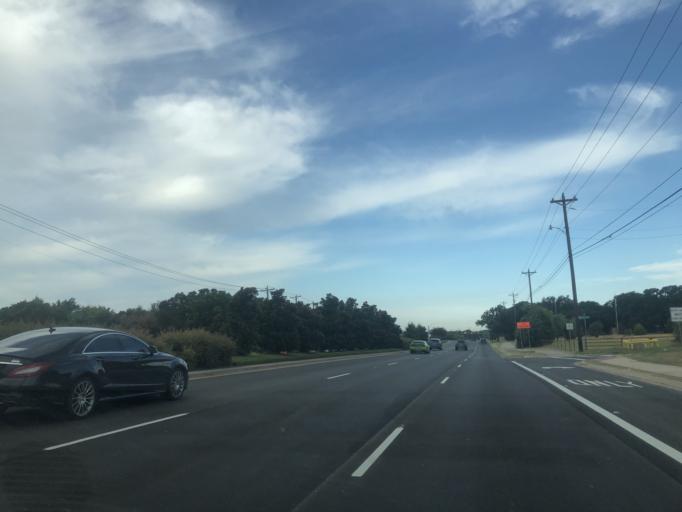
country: US
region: Texas
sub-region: Tarrant County
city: Southlake
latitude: 32.9352
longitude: -97.1919
